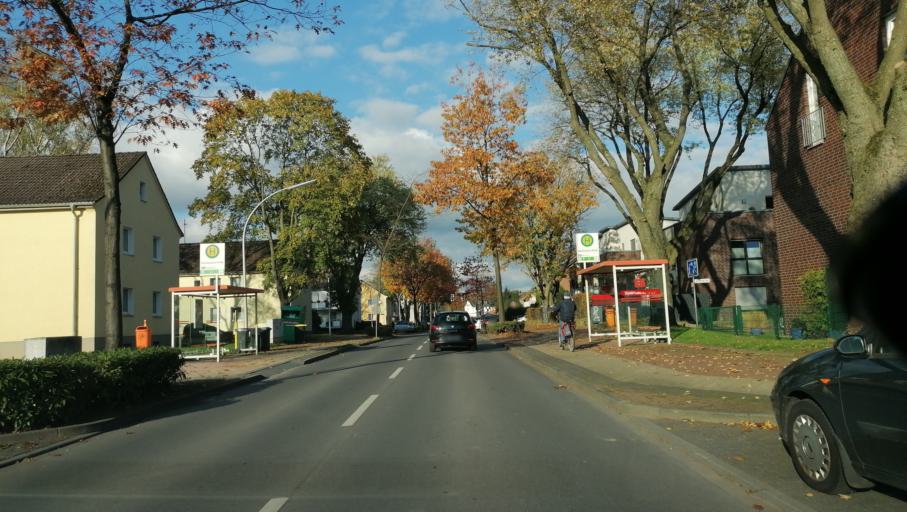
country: DE
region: North Rhine-Westphalia
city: Datteln
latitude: 51.6540
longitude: 7.3307
